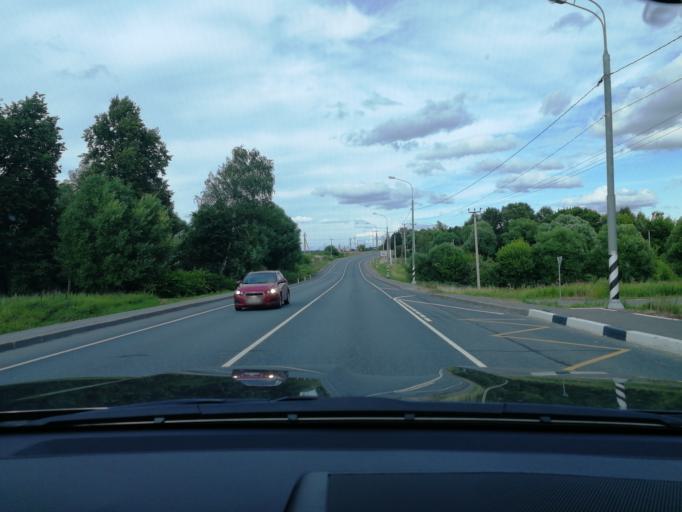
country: RU
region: Moskovskaya
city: Popovo
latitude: 55.0713
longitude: 37.8099
